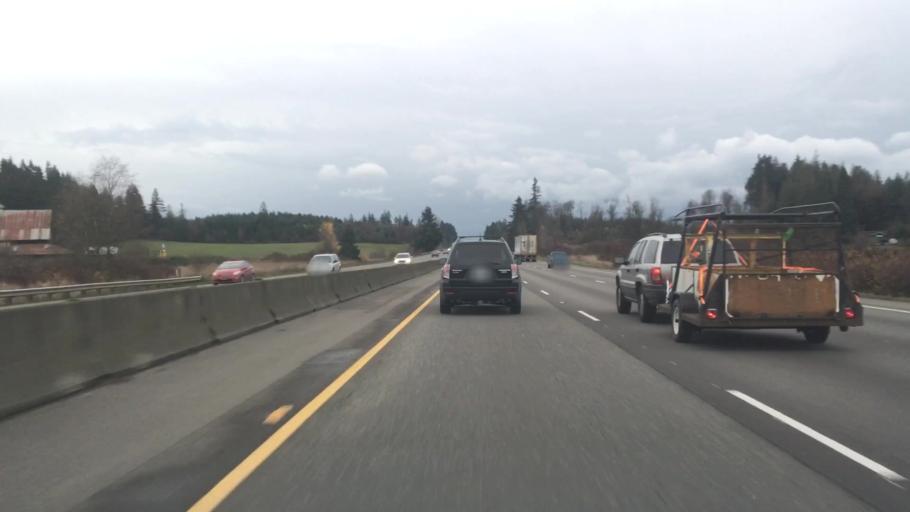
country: US
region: Washington
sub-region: Thurston County
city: Tumwater
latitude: 46.9159
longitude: -122.9501
